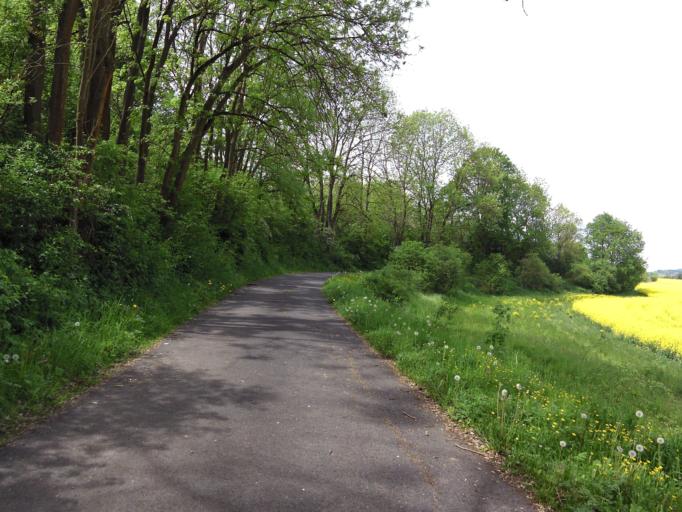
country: DE
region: Thuringia
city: Ifta
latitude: 51.0500
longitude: 10.2046
